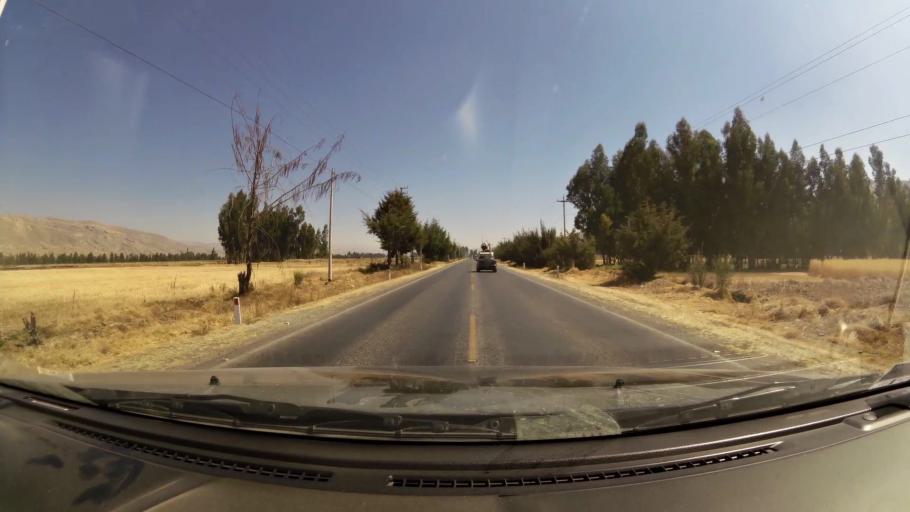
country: PE
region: Junin
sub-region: Provincia de Jauja
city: Huamali
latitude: -11.8213
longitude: -75.4139
